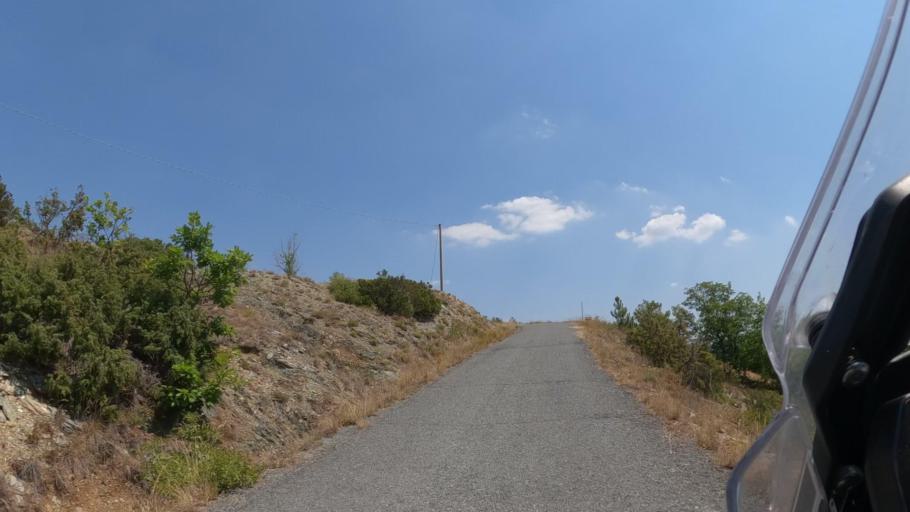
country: IT
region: Piedmont
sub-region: Provincia di Alessandria
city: Ponzone
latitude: 44.5433
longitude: 8.4762
